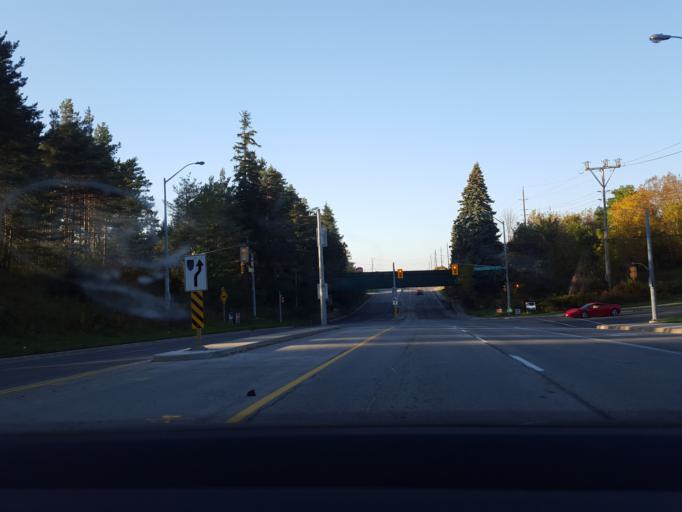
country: CA
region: Ontario
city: Newmarket
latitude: 43.9803
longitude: -79.4629
